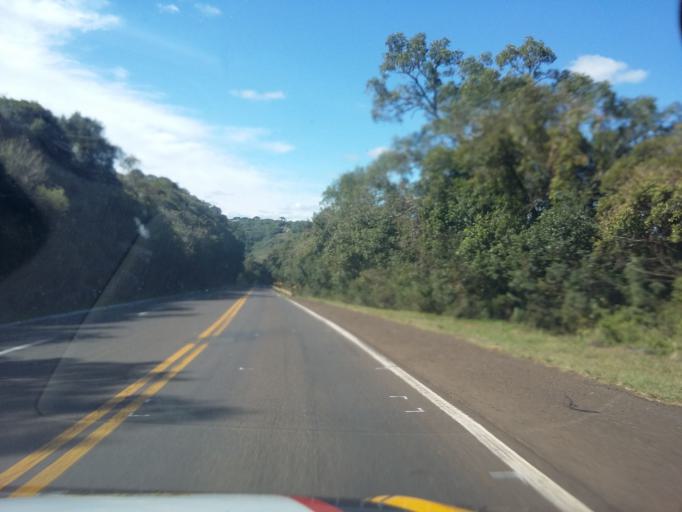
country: BR
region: Rio Grande do Sul
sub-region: Vacaria
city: Vacaria
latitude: -28.5776
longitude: -51.0191
